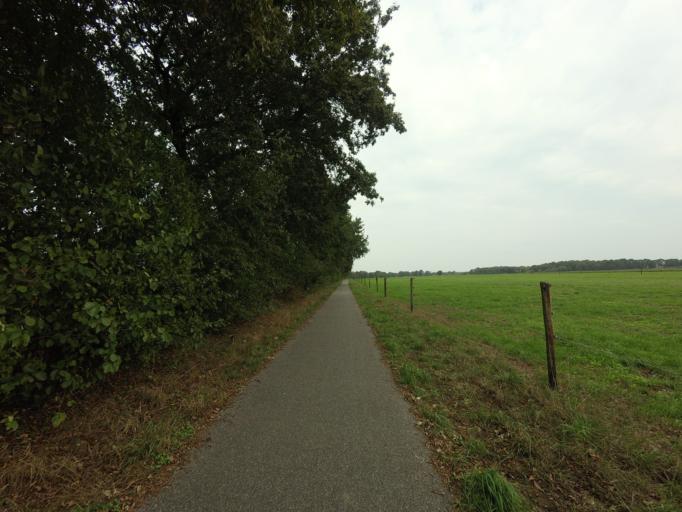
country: NL
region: Drenthe
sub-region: Gemeente Assen
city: Assen
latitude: 53.0014
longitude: 6.6346
